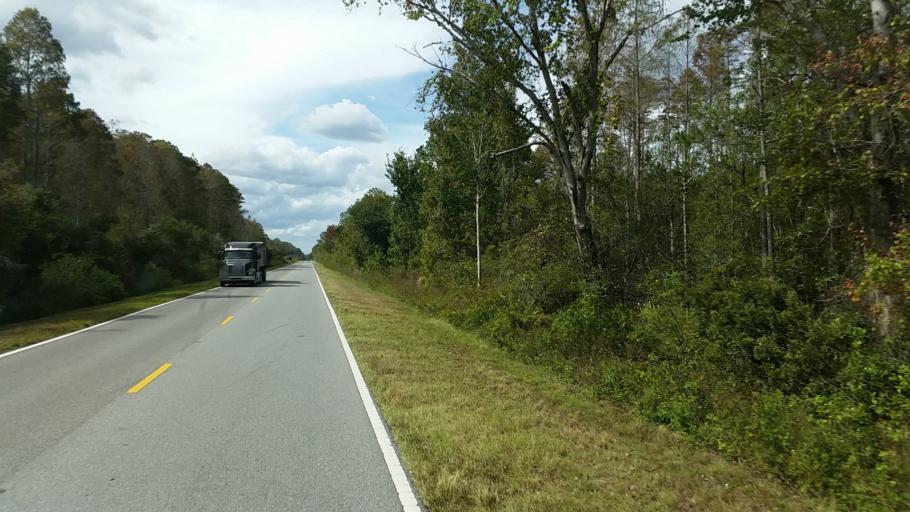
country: US
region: Florida
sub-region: Lake County
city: Four Corners
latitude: 28.3756
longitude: -81.7639
